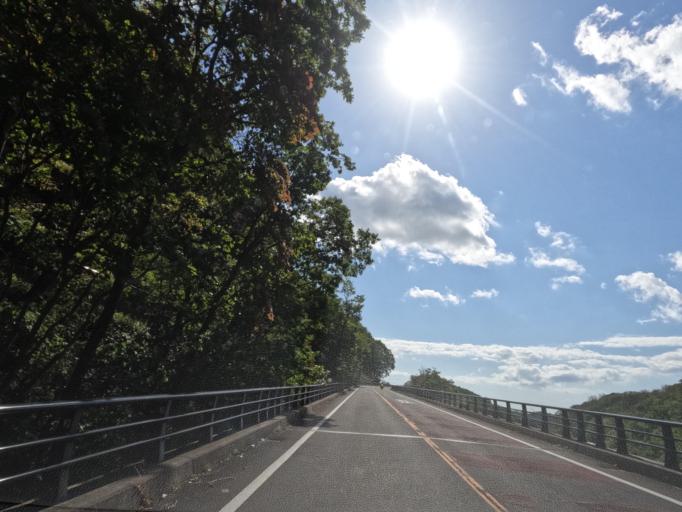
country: JP
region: Hokkaido
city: Shiraoi
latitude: 42.4802
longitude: 141.1450
